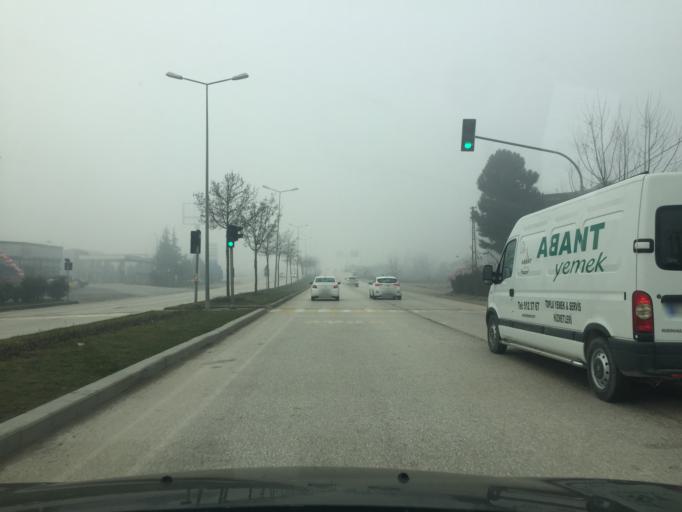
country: TR
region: Duzce
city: Duzce
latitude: 40.8403
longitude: 31.1786
